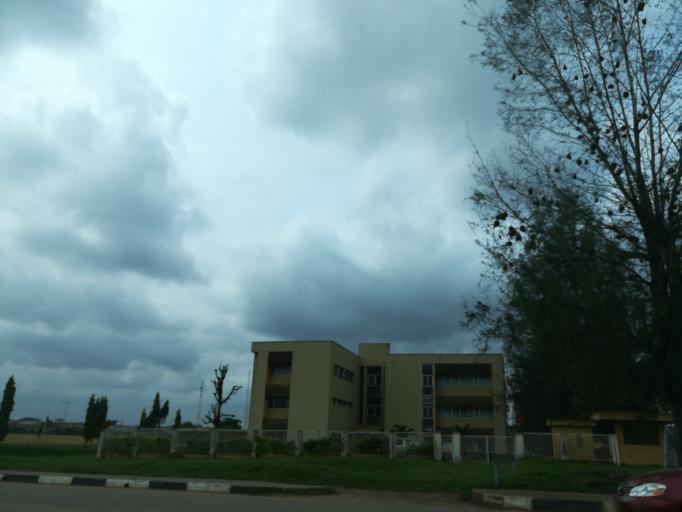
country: NG
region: Lagos
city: Oshodi
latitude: 6.5668
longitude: 3.3230
